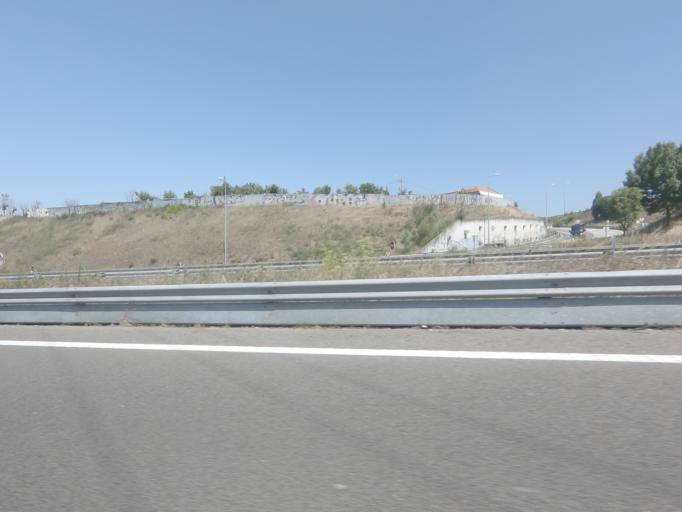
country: PT
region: Porto
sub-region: Matosinhos
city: Guifoes
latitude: 41.2025
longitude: -8.6514
